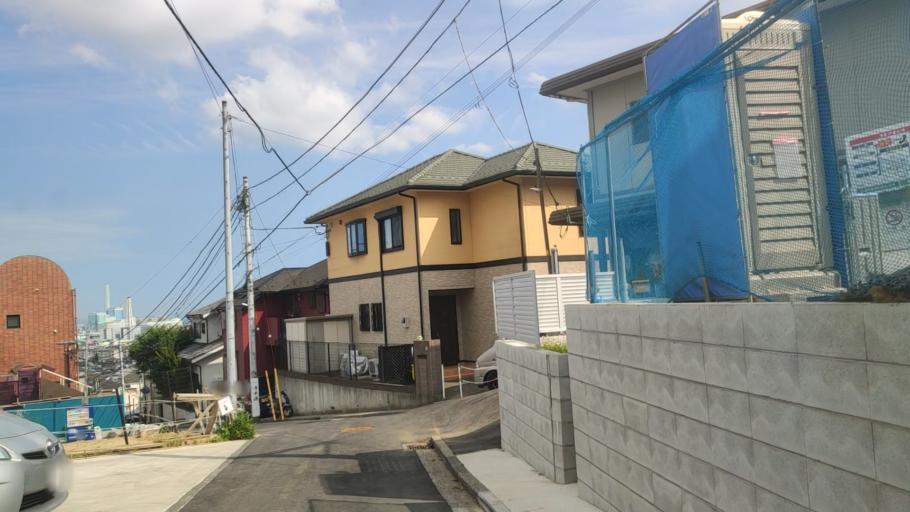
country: JP
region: Kanagawa
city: Yokohama
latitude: 35.4214
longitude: 139.6131
